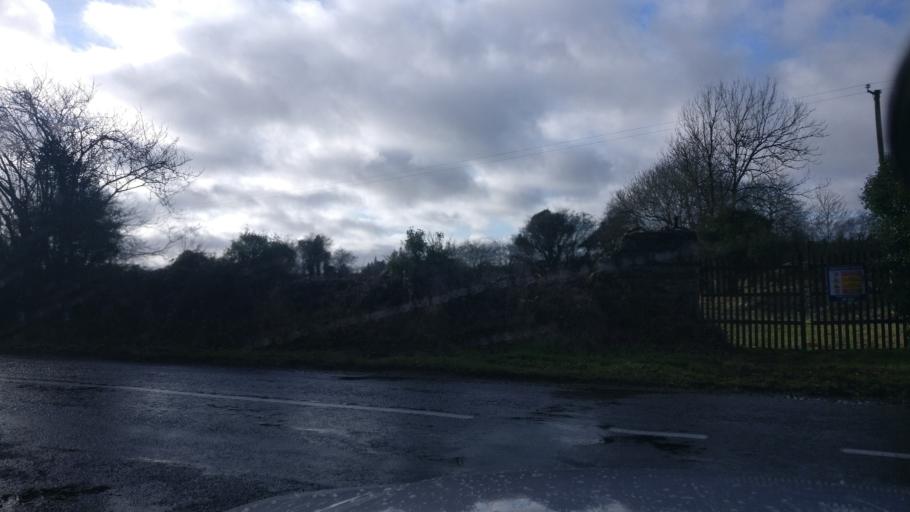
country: IE
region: Connaught
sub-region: County Galway
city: Loughrea
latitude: 53.2496
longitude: -8.6226
